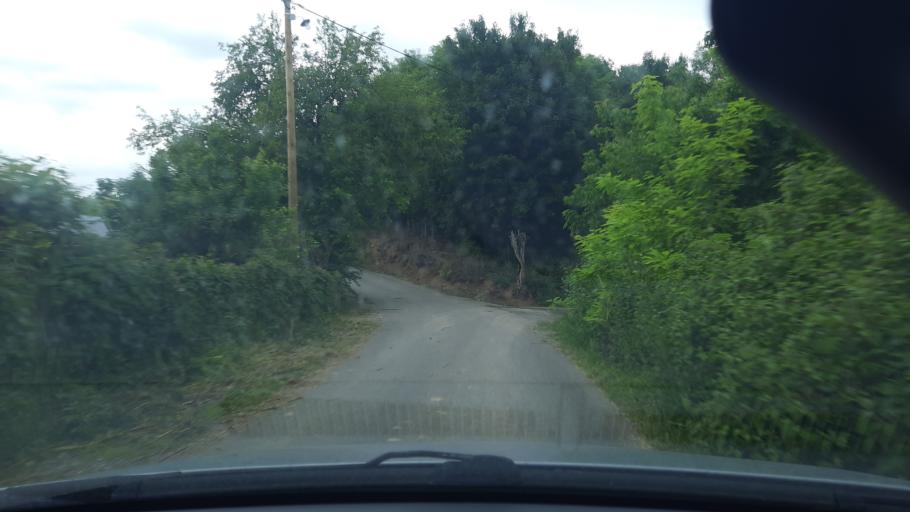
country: RS
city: Jarebice
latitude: 44.4966
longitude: 19.4771
